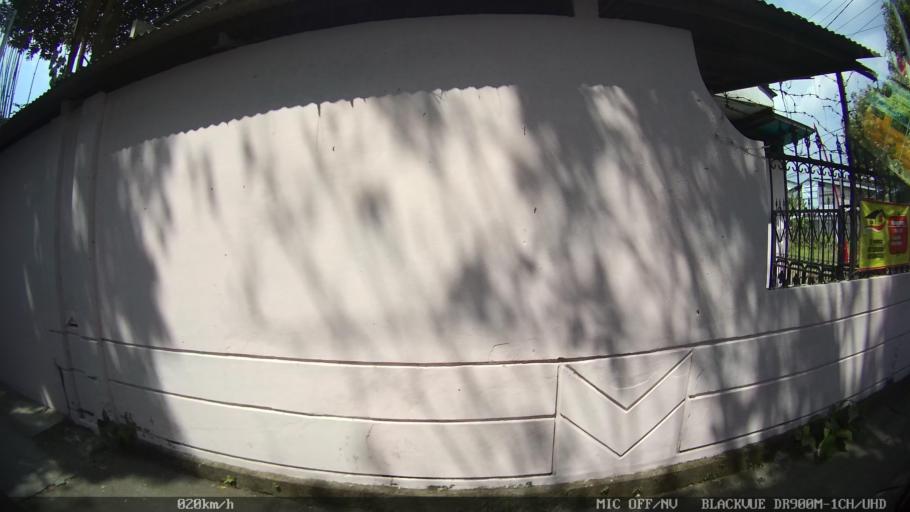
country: ID
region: Daerah Istimewa Yogyakarta
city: Depok
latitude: -7.8078
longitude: 110.4070
